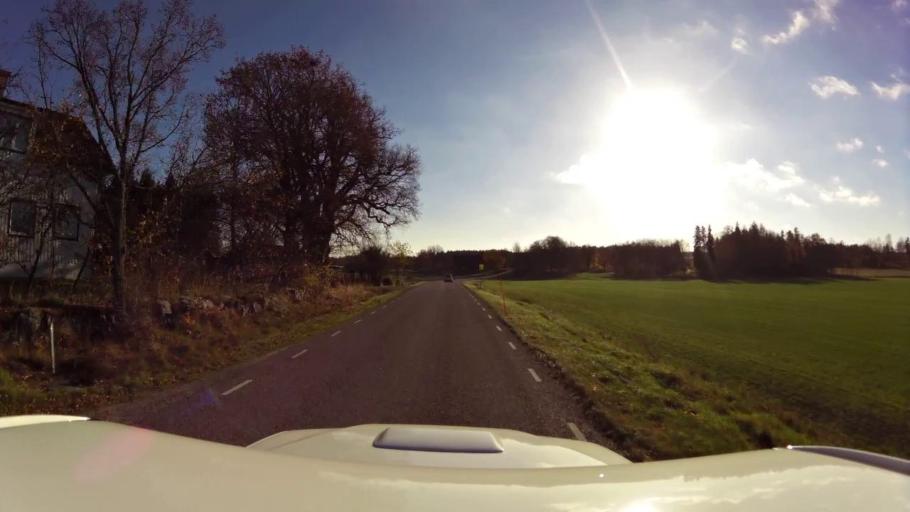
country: SE
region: OEstergoetland
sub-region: Linkopings Kommun
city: Linghem
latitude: 58.4655
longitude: 15.7708
